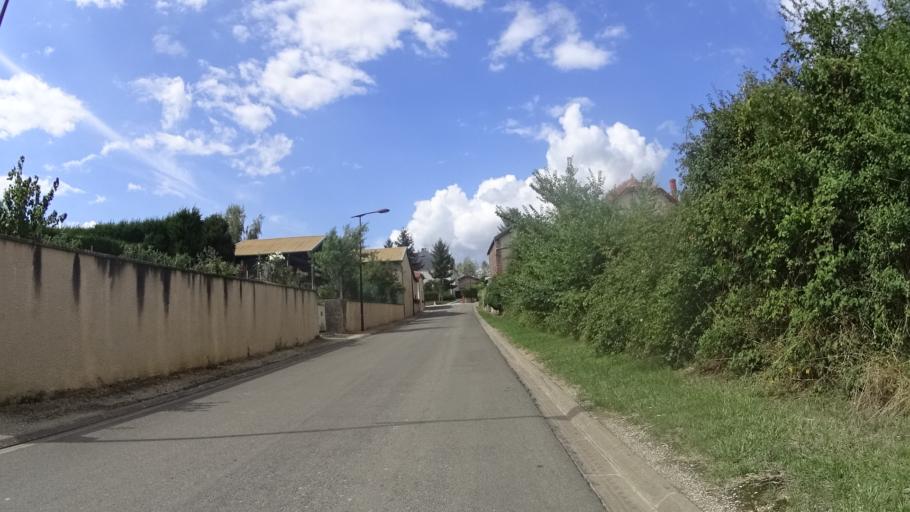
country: FR
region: Champagne-Ardenne
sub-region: Departement de la Marne
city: Pargny-sur-Saulx
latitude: 48.6936
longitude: 4.8029
